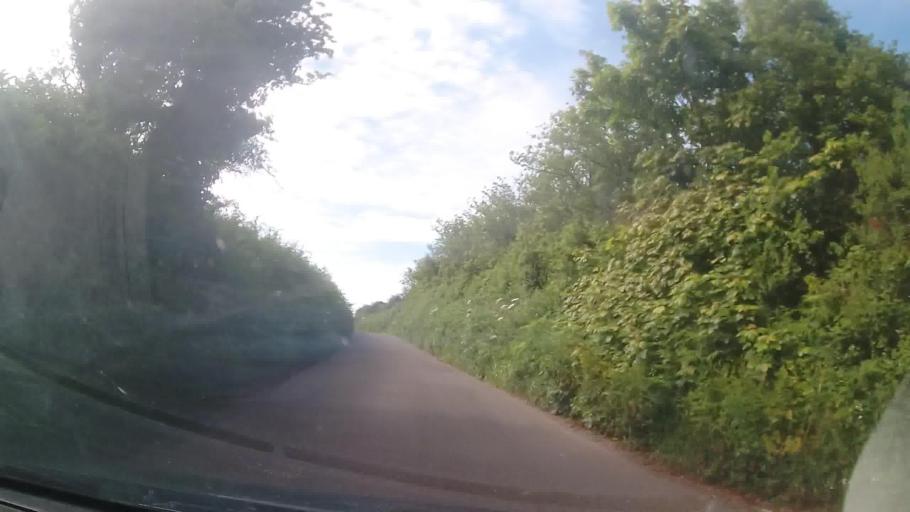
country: GB
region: England
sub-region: Devon
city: Salcombe
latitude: 50.2425
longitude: -3.6798
